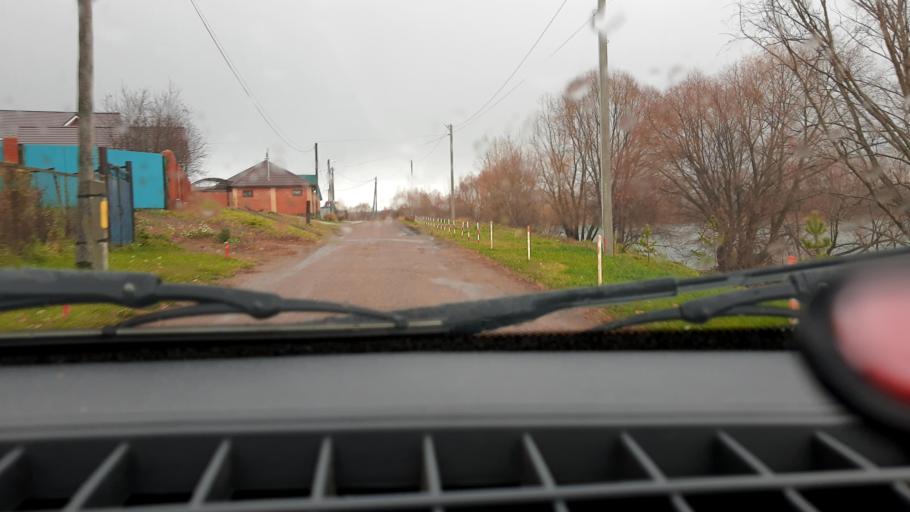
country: RU
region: Bashkortostan
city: Ufa
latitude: 54.8190
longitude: 55.9893
